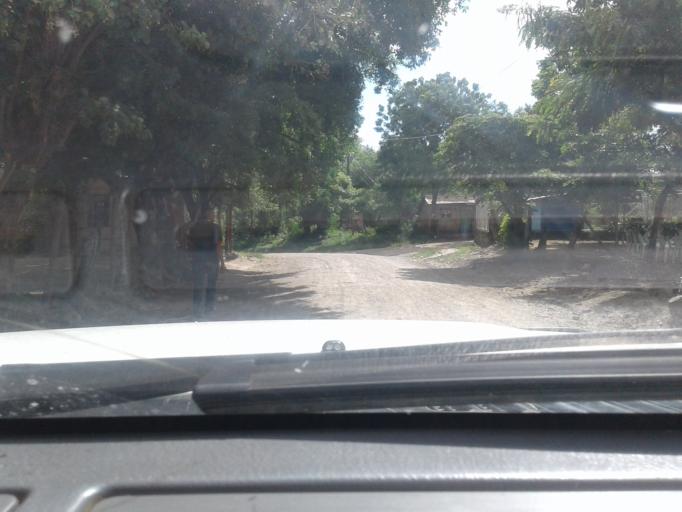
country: NI
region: Matagalpa
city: Ciudad Dario
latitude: 12.8457
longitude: -86.1217
